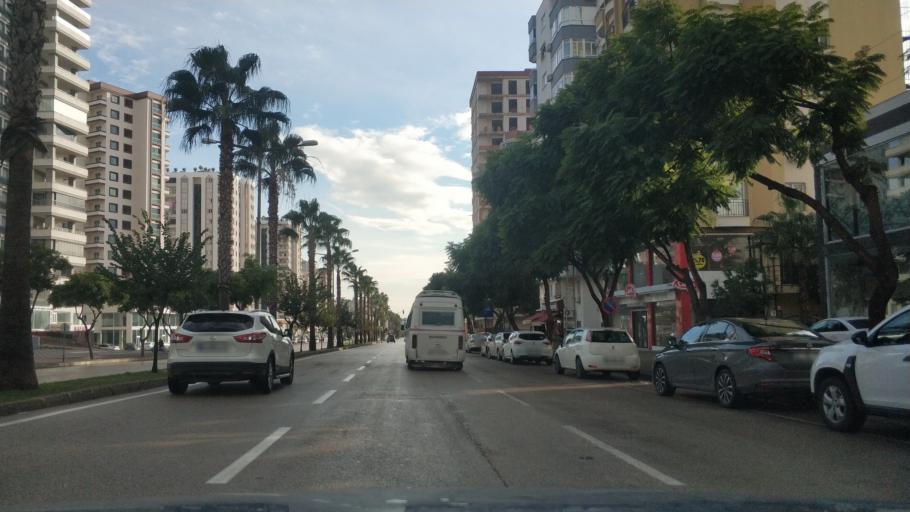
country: TR
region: Adana
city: Seyhan
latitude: 37.0458
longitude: 35.2717
